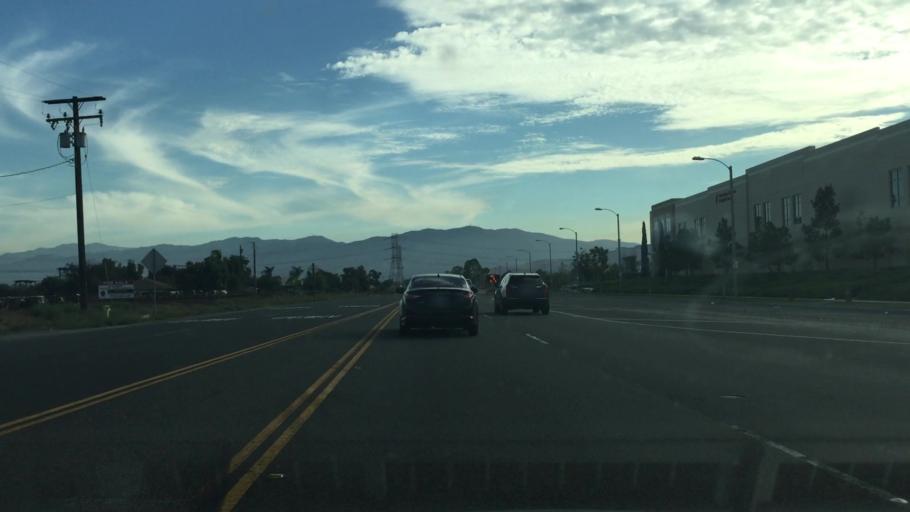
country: US
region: California
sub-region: San Bernardino County
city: Los Serranos
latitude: 33.9593
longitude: -117.6506
